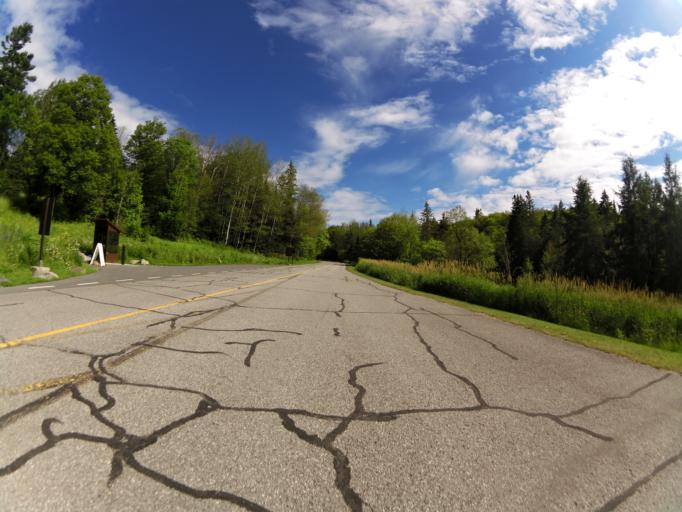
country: CA
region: Quebec
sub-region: Outaouais
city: Wakefield
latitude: 45.6266
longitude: -76.0136
